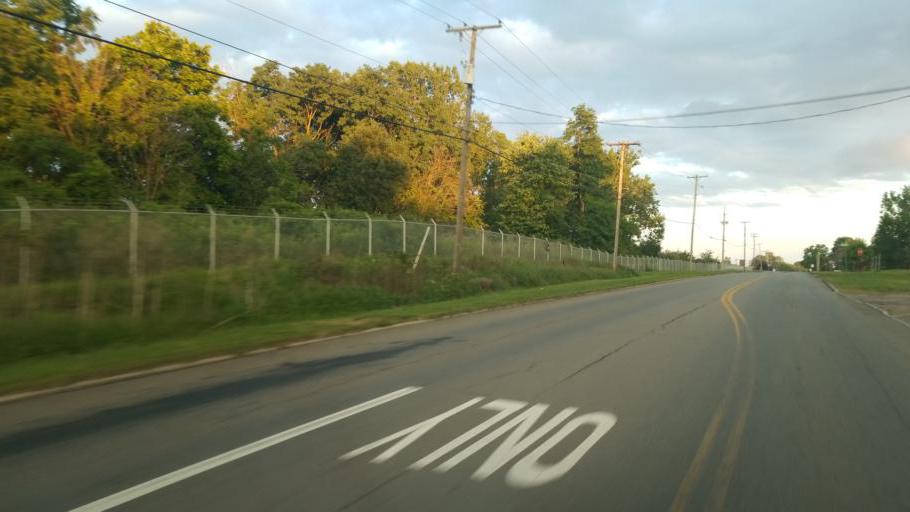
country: US
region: Ohio
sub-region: Richland County
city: Mansfield
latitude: 40.7877
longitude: -82.5263
